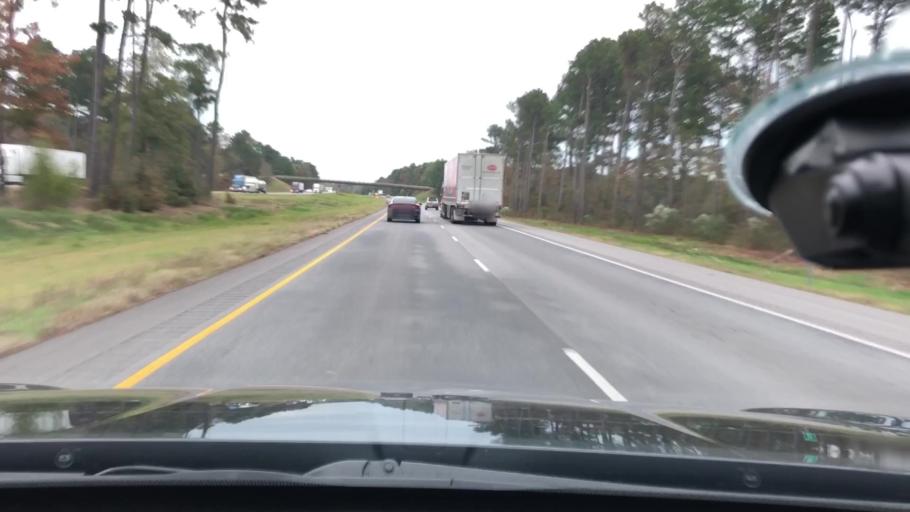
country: US
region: Arkansas
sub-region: Hempstead County
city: Hope
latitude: 33.6288
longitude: -93.7324
